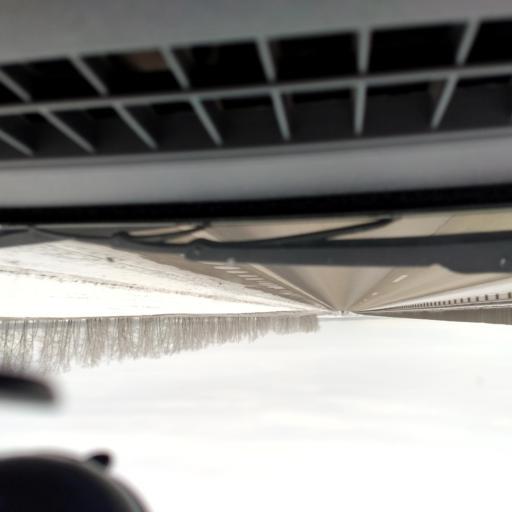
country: RU
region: Bashkortostan
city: Kushnarenkovo
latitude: 55.0965
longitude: 55.2451
